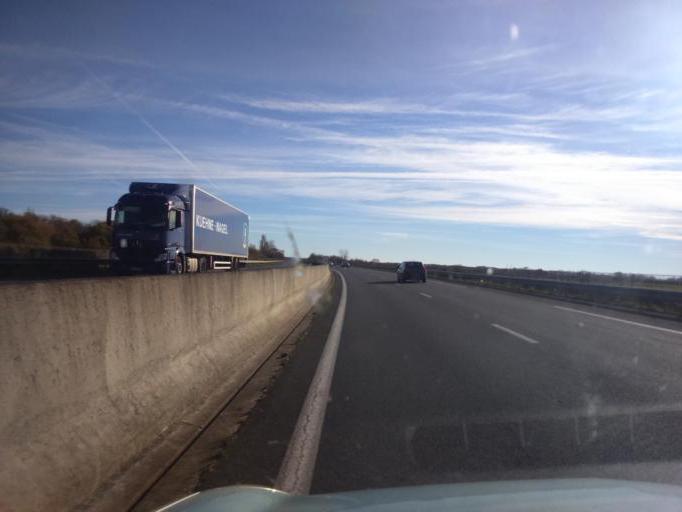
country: FR
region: Poitou-Charentes
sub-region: Departement de la Charente-Maritime
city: Saint-Laurent-de-la-Pree
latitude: 45.9808
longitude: -1.0125
